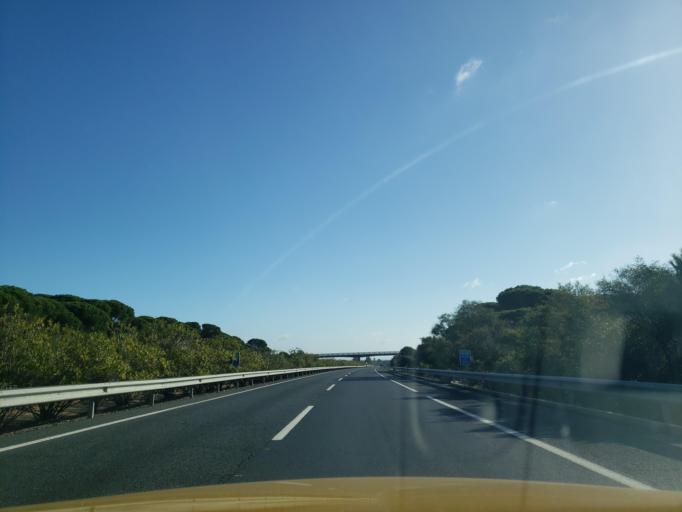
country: ES
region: Andalusia
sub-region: Provincia de Huelva
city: Cartaya
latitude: 37.3228
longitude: -7.0975
